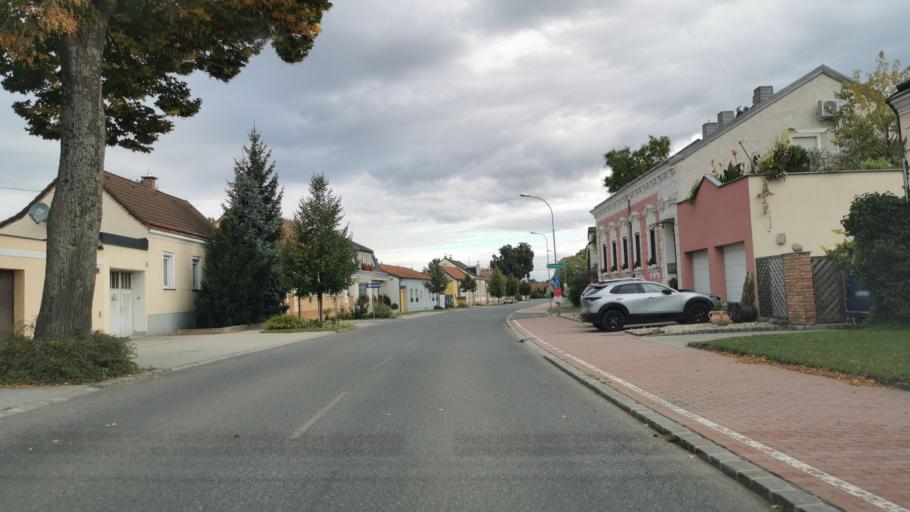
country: AT
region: Lower Austria
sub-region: Politischer Bezirk Ganserndorf
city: Obersiebenbrunn
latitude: 48.2610
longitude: 16.7019
